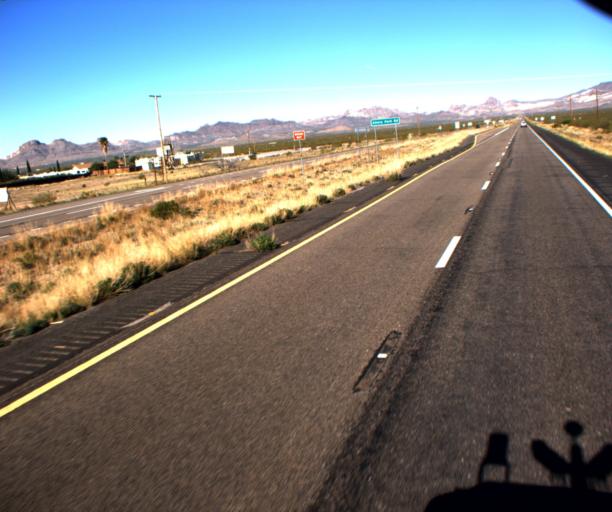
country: US
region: Arizona
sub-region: Mohave County
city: Golden Valley
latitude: 35.2258
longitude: -114.2907
